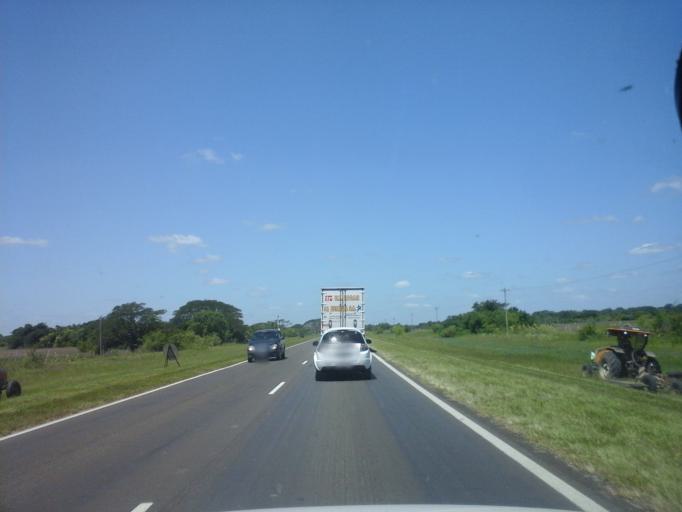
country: AR
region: Corrientes
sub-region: Departamento de Itati
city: Itati
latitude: -27.3420
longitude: -58.2181
